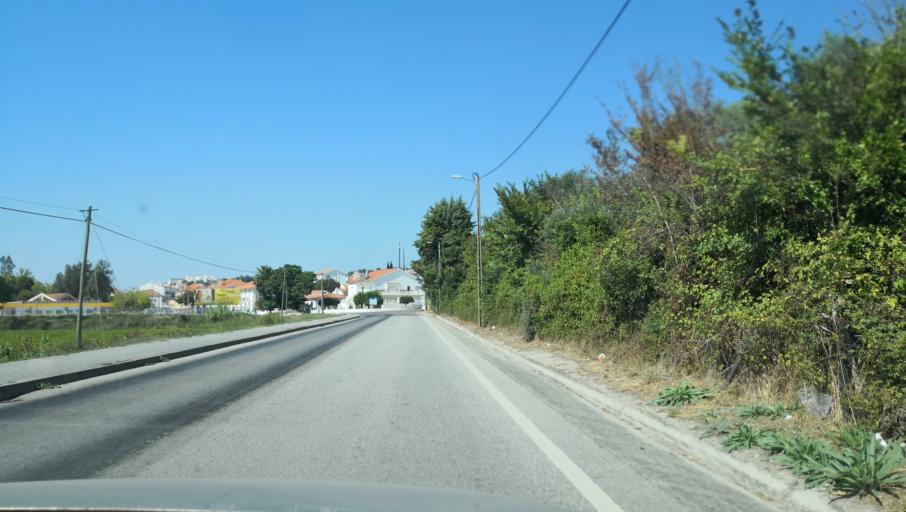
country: PT
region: Setubal
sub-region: Alcacer do Sal
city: Alcacer do Sal
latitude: 38.3692
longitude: -8.4980
